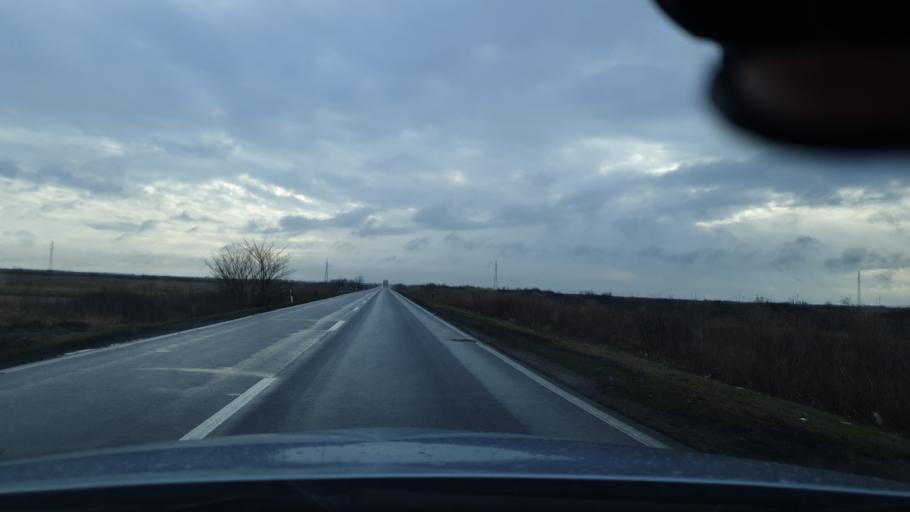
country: RS
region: Autonomna Pokrajina Vojvodina
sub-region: Juznobanatski Okrug
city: Kovin
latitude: 44.8005
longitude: 20.9031
